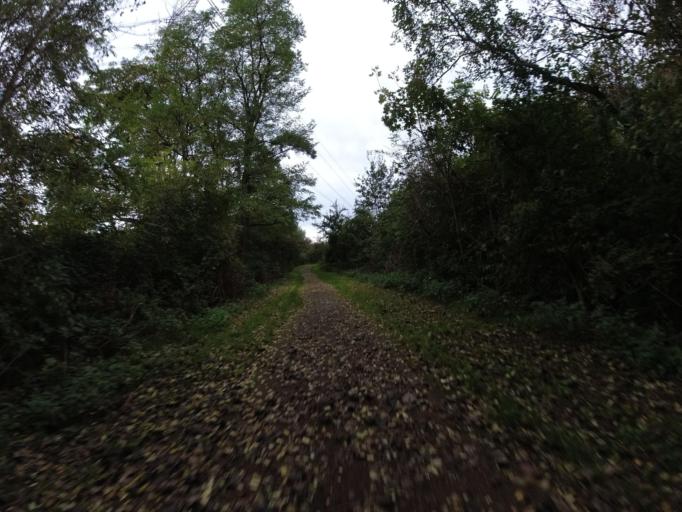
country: DE
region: North Rhine-Westphalia
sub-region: Regierungsbezirk Dusseldorf
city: Hochfeld
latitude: 51.3924
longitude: 6.6823
